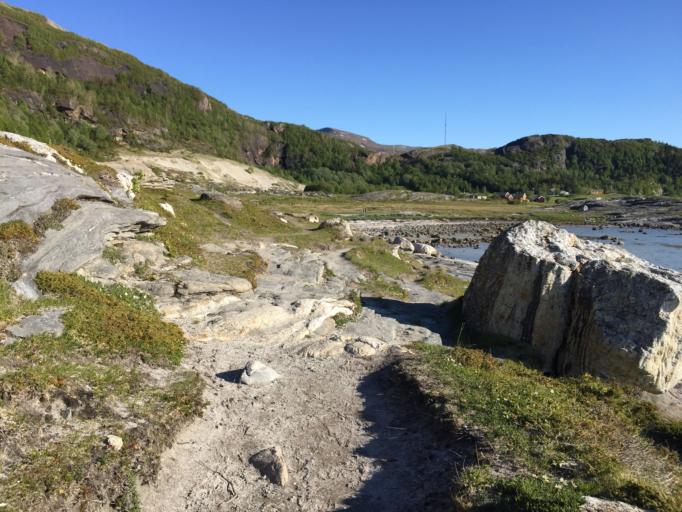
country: NO
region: Nordland
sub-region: Bodo
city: Loding
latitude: 67.4147
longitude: 14.6326
